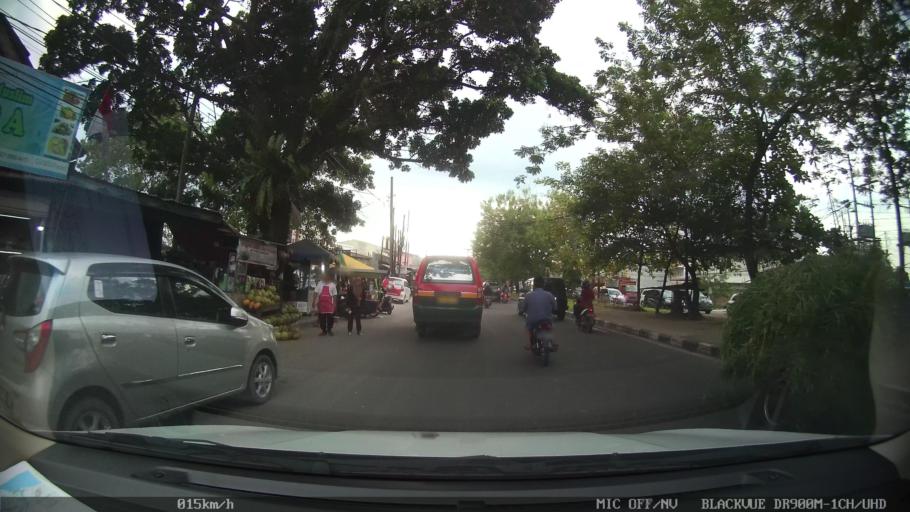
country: ID
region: North Sumatra
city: Deli Tua
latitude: 3.5411
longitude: 98.6607
